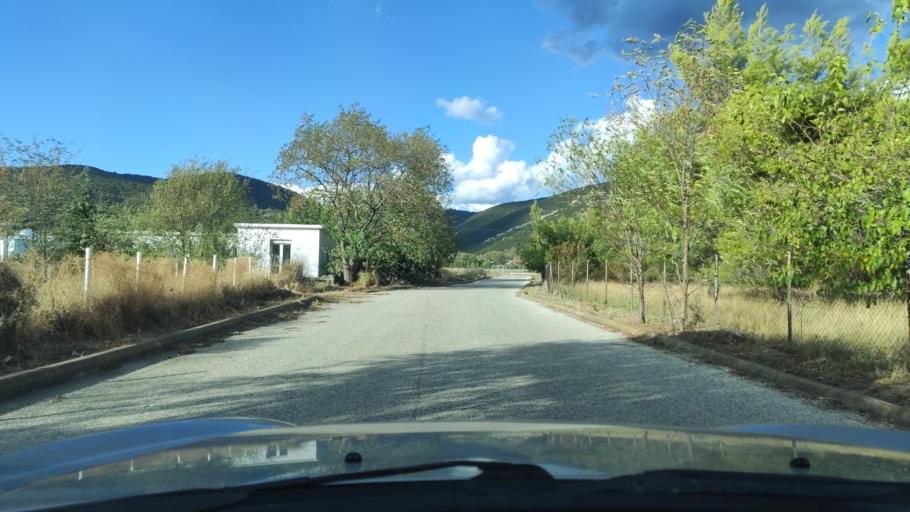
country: GR
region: East Macedonia and Thrace
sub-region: Nomos Xanthis
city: Selero
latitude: 41.1240
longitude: 25.0626
